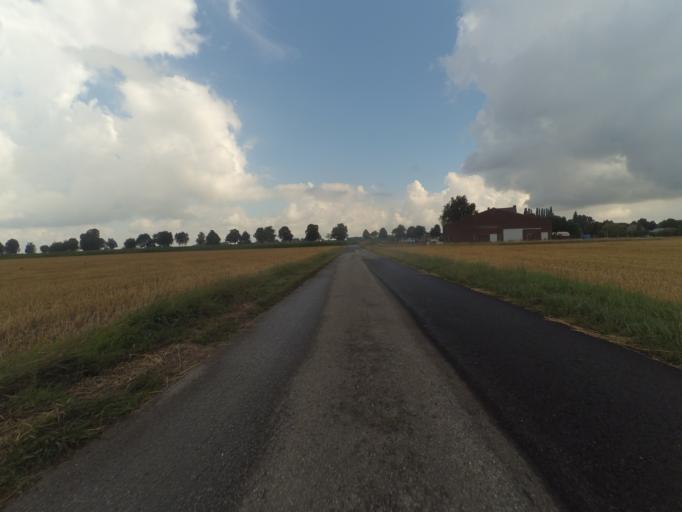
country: NL
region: Limburg
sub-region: Gemeente Schinnen
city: Doenrade
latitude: 50.9936
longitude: 5.9119
